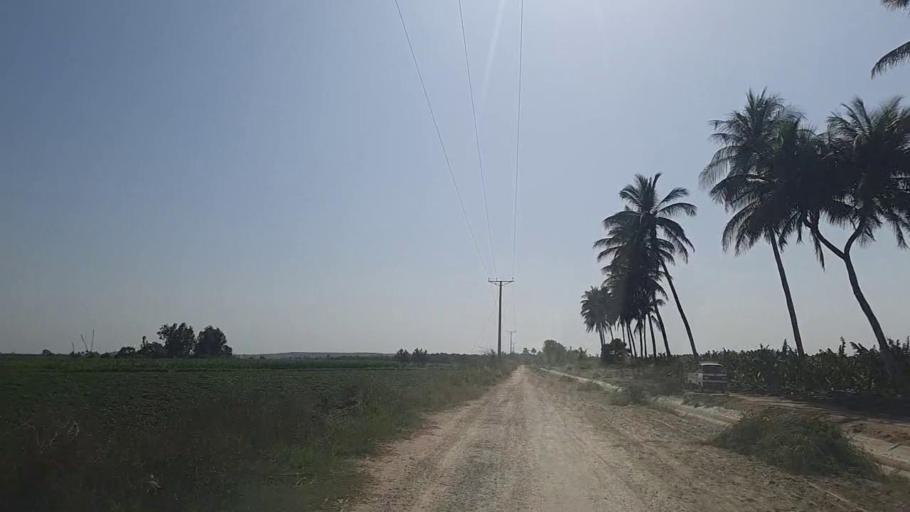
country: PK
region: Sindh
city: Thatta
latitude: 24.6334
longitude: 67.8832
